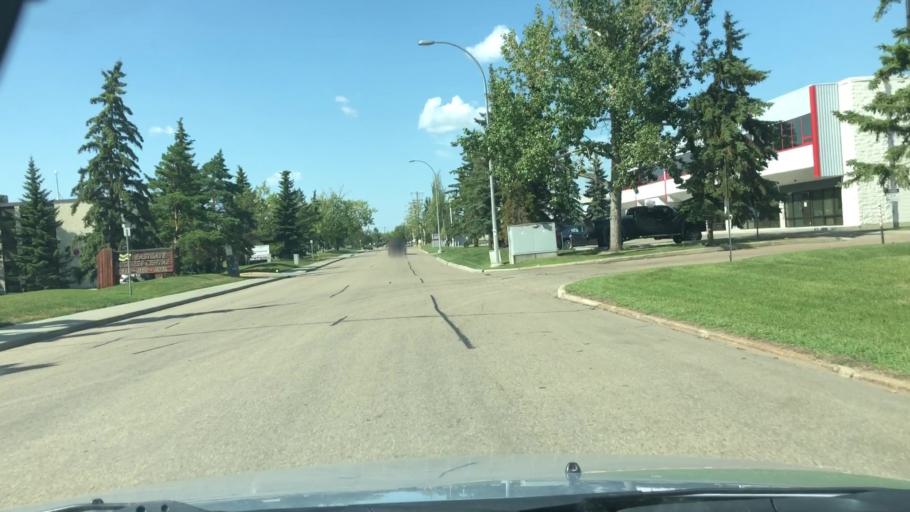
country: CA
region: Alberta
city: Edmonton
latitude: 53.5317
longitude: -113.4149
